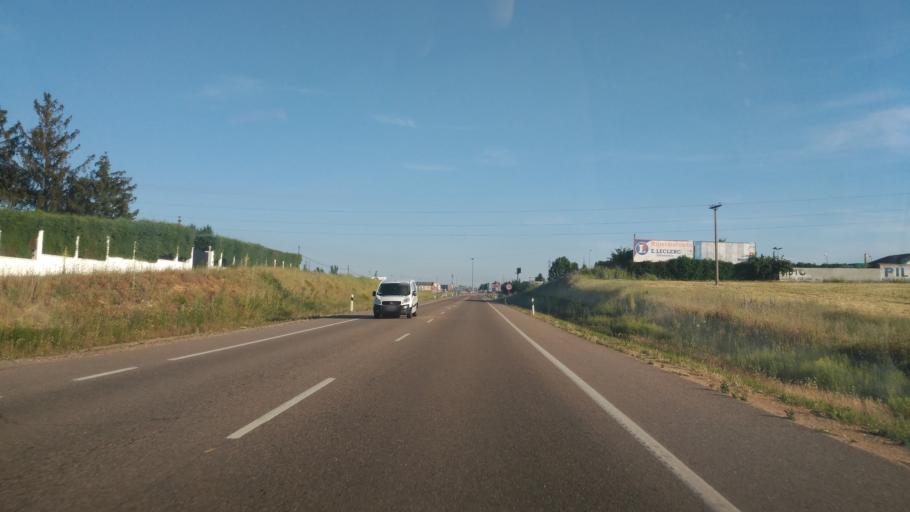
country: ES
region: Castille and Leon
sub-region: Provincia de Salamanca
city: Villares de la Reina
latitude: 41.0059
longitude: -5.6680
